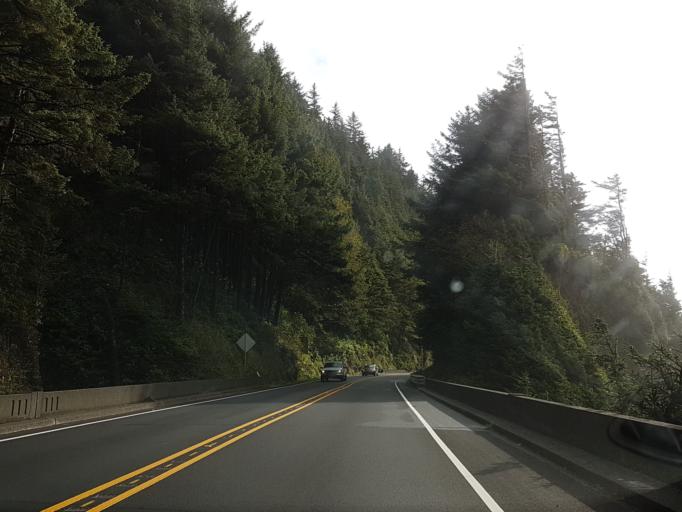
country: US
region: Oregon
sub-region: Lane County
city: Florence
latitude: 44.1280
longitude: -124.1231
